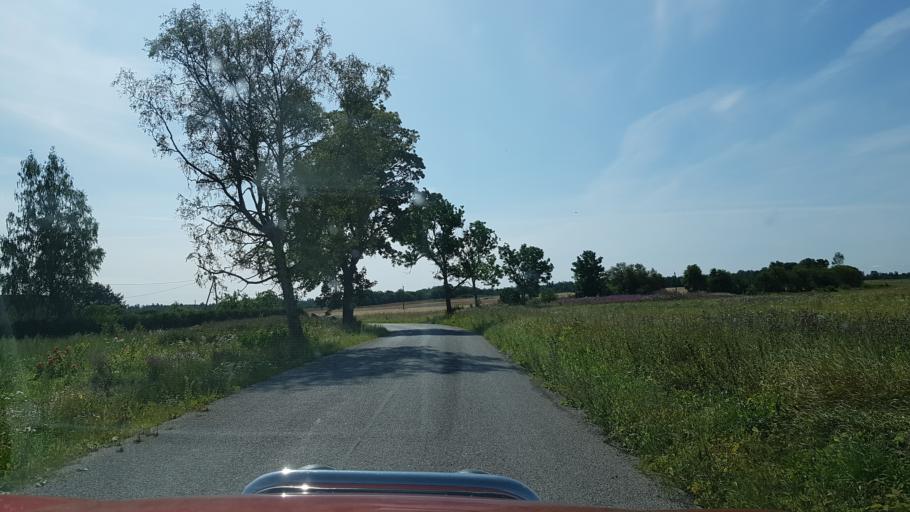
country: EE
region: Jaervamaa
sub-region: Jaerva-Jaani vald
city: Jarva-Jaani
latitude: 59.0864
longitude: 25.7525
